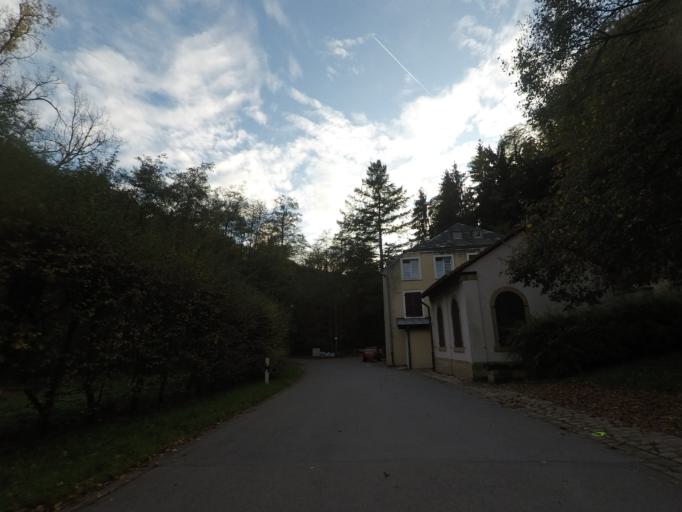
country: LU
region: Luxembourg
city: Kirchberg
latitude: 49.6042
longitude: 6.1587
